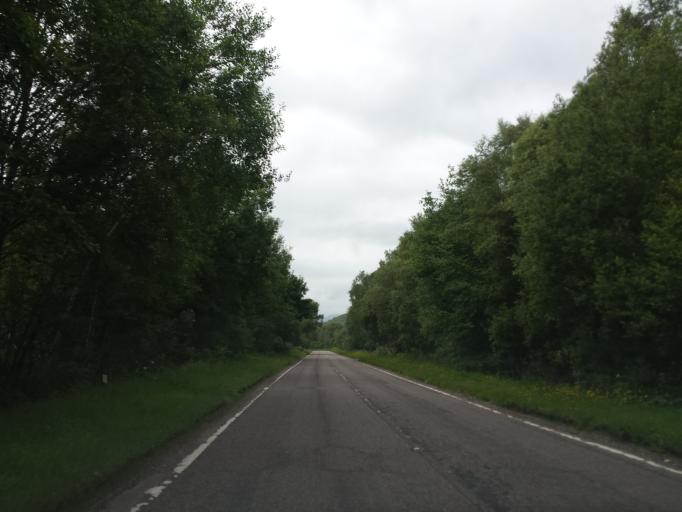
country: GB
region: Scotland
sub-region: Highland
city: Fort William
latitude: 56.8544
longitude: -5.2631
